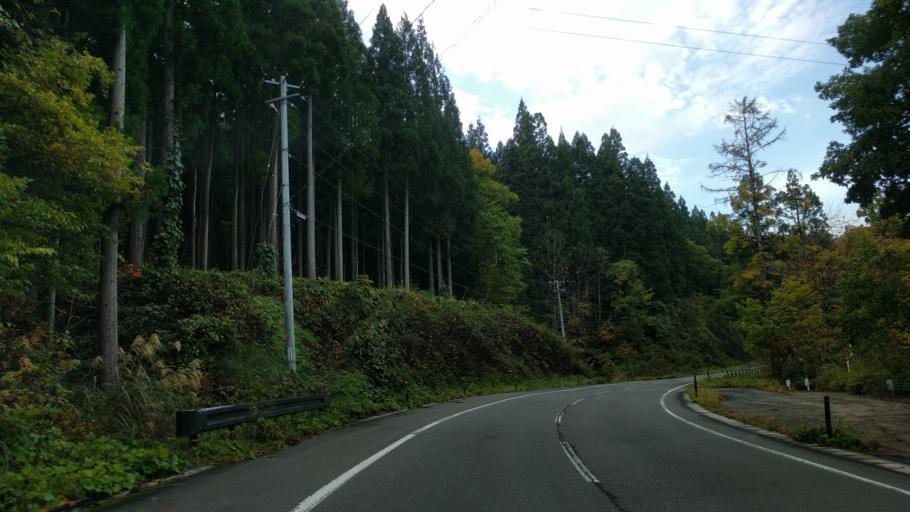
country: JP
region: Fukushima
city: Kitakata
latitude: 37.3987
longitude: 139.6953
